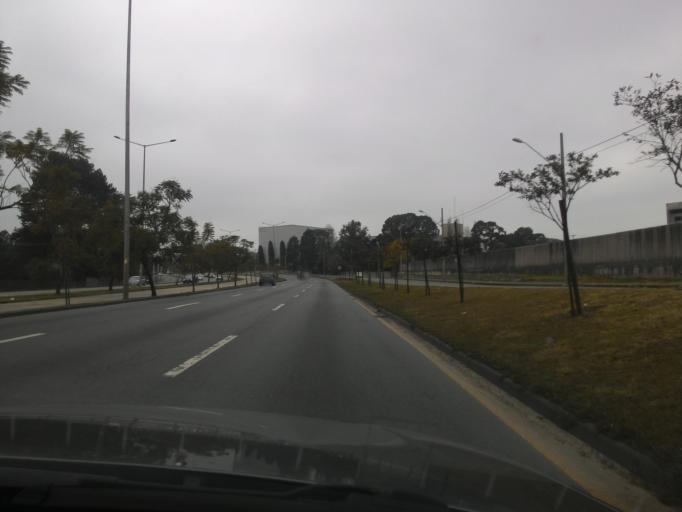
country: BR
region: Parana
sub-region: Curitiba
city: Curitiba
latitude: -25.4522
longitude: -49.2398
